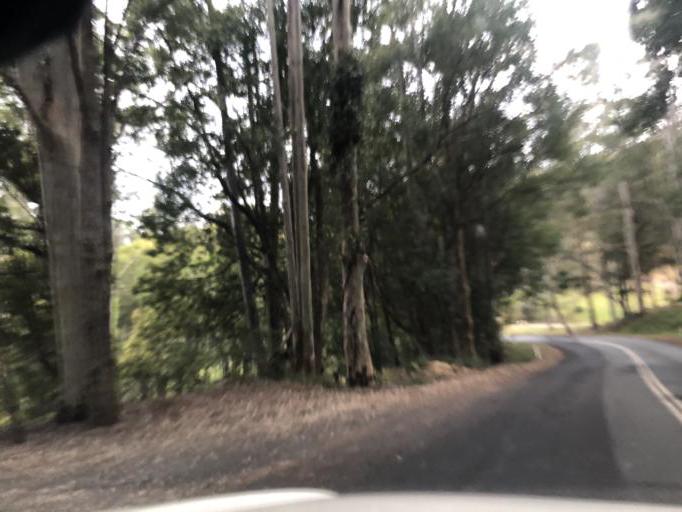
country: AU
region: New South Wales
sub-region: Coffs Harbour
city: Boambee
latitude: -30.2585
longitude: 153.0312
